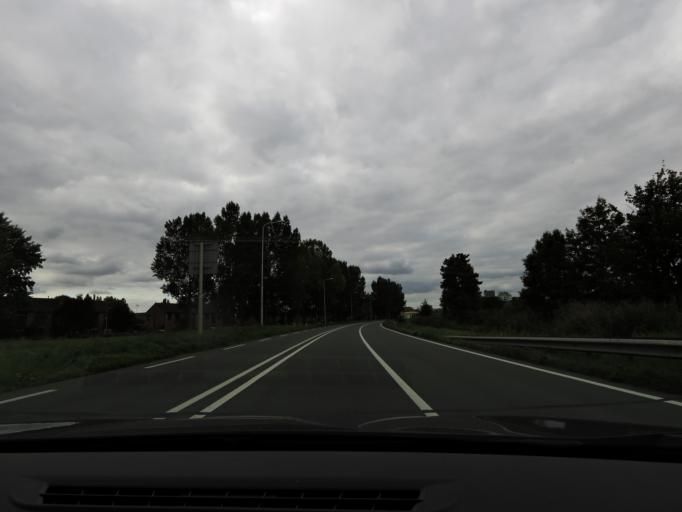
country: NL
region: South Holland
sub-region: Gemeente Krimpen aan den IJssel
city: Krimpen aan den IJssel
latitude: 51.9078
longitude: 4.5964
